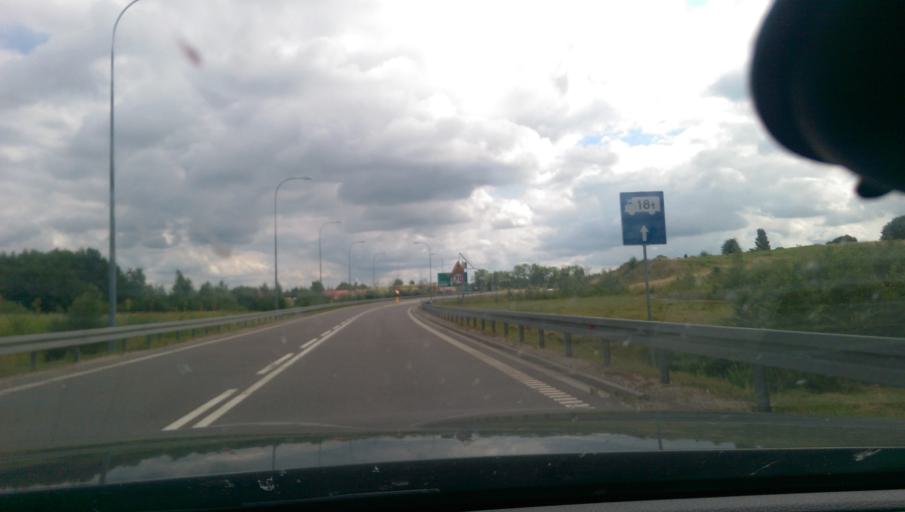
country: PL
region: Warmian-Masurian Voivodeship
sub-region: Powiat goldapski
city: Goldap
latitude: 54.2986
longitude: 22.3065
